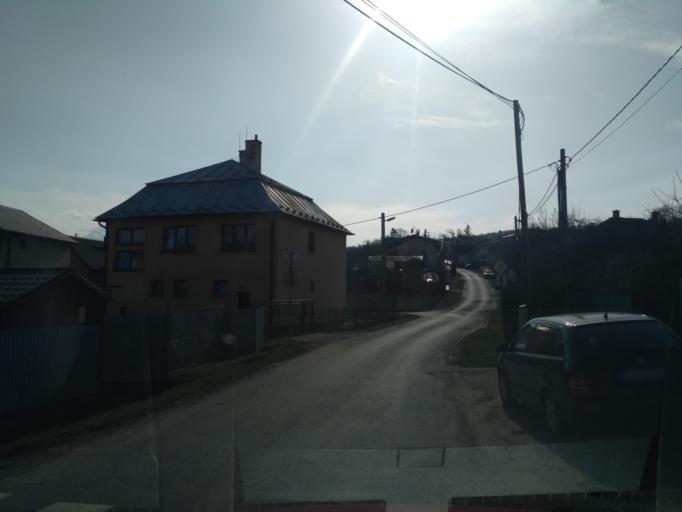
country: SK
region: Kosicky
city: Kosice
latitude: 48.6909
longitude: 21.1916
